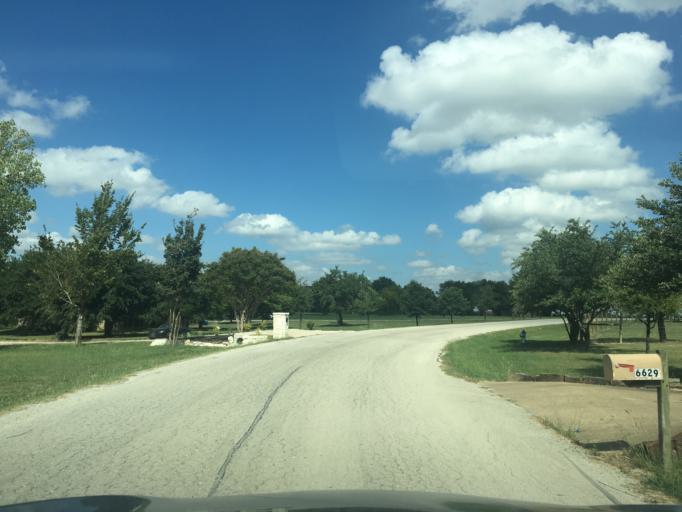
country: US
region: Texas
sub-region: Dallas County
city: Sachse
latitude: 32.9514
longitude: -96.5599
